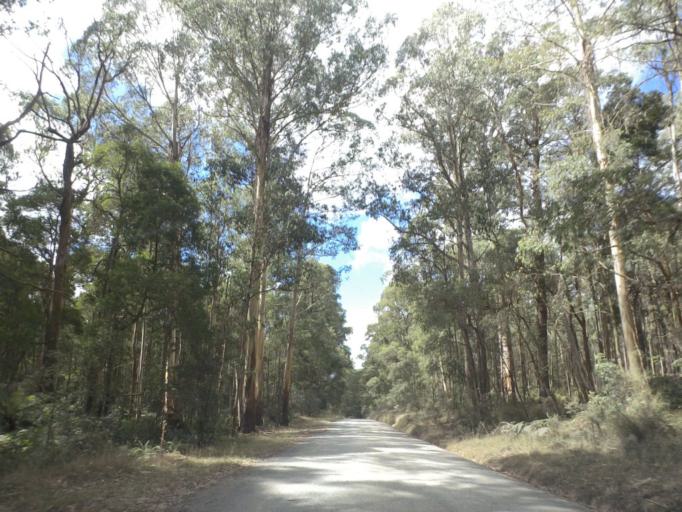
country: AU
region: Victoria
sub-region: Yarra Ranges
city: Millgrove
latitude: -37.5416
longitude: 145.9253
